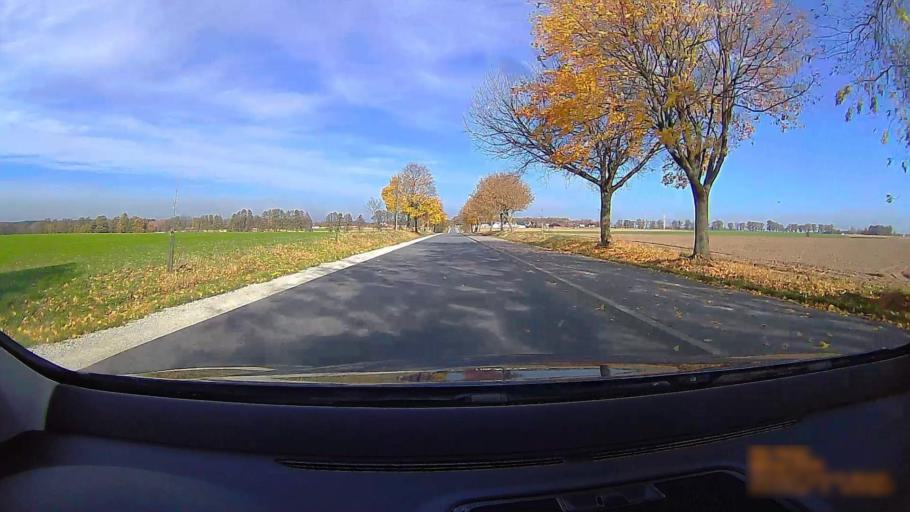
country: PL
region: Greater Poland Voivodeship
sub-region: Powiat kepinski
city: Kepno
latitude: 51.3509
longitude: 18.0269
